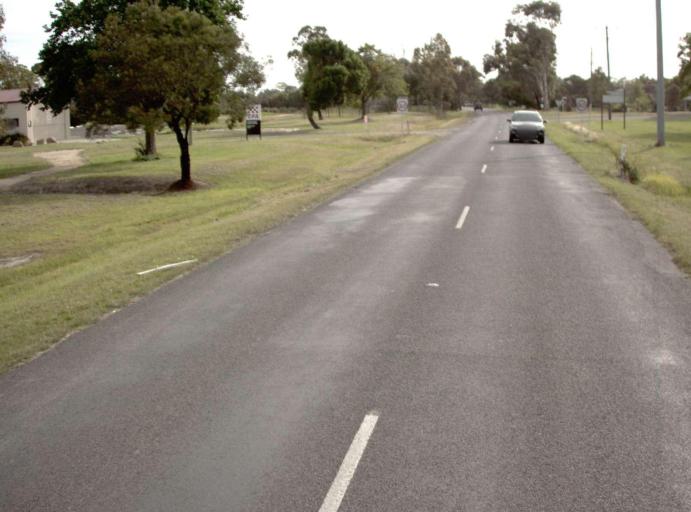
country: AU
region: Victoria
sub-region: Latrobe
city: Traralgon
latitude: -38.0609
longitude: 146.6236
